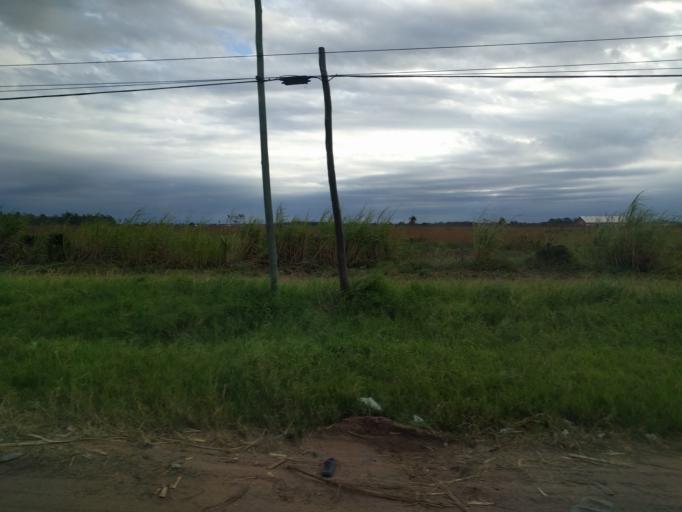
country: BO
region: Santa Cruz
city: Warnes
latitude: -17.5517
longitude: -63.1600
